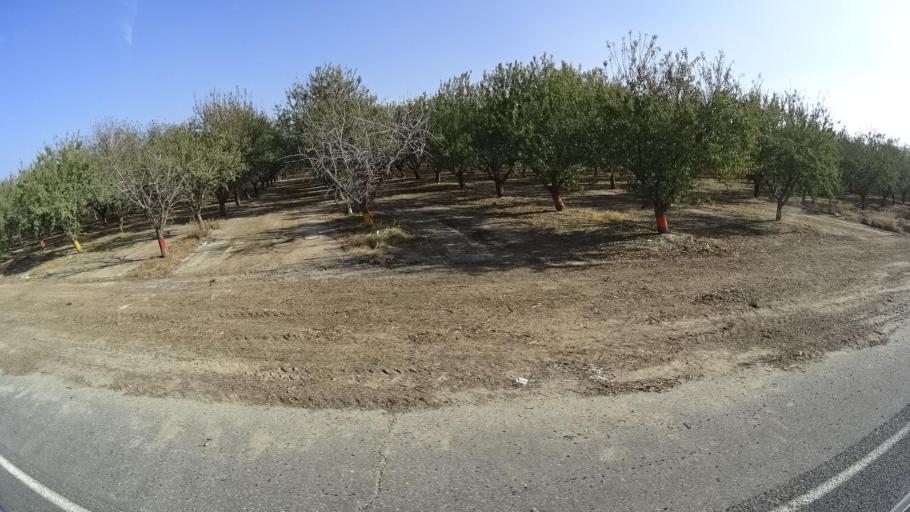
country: US
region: California
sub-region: Kern County
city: McFarland
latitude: 35.6447
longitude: -119.2012
